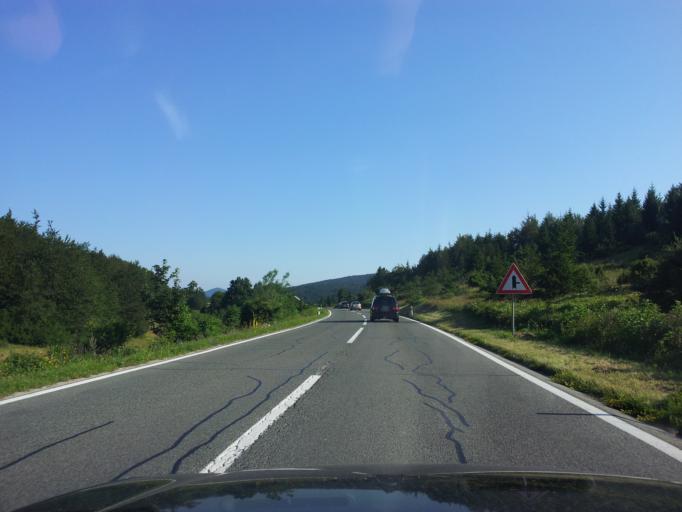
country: HR
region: Licko-Senjska
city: Jezerce
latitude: 44.8047
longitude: 15.6834
